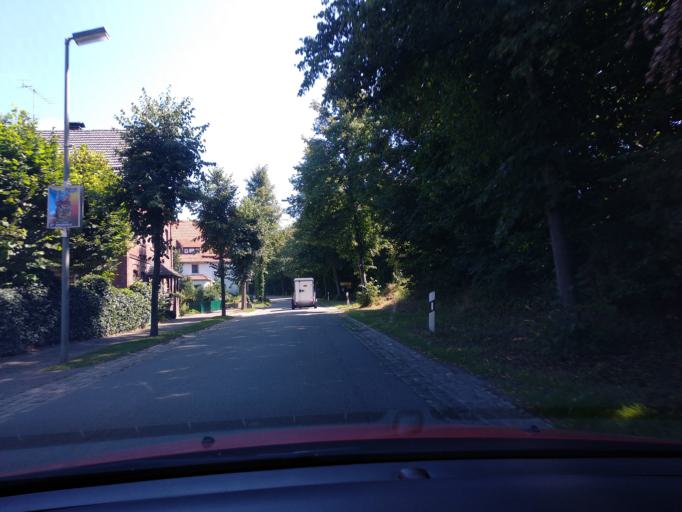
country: DE
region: North Rhine-Westphalia
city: Brakel
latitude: 51.6544
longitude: 9.1230
